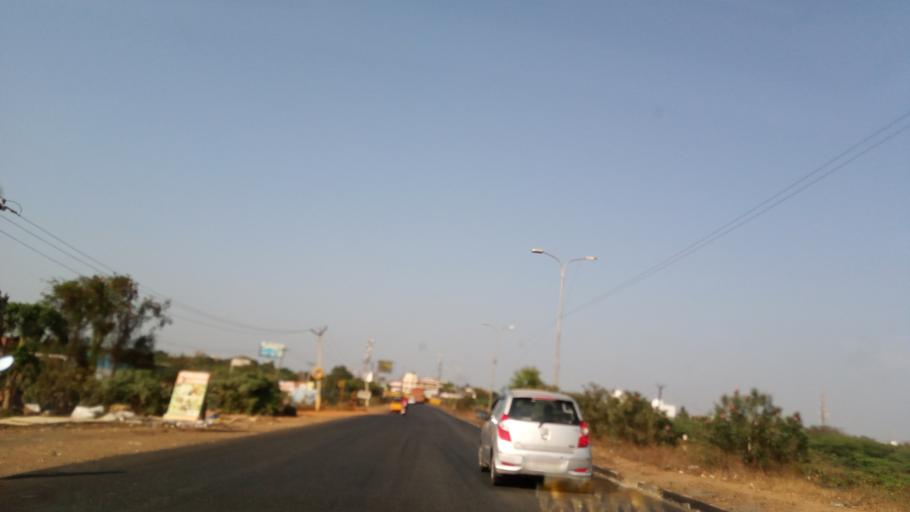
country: IN
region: Tamil Nadu
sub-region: Kancheepuram
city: Sriperumbudur
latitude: 12.9923
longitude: 79.9857
